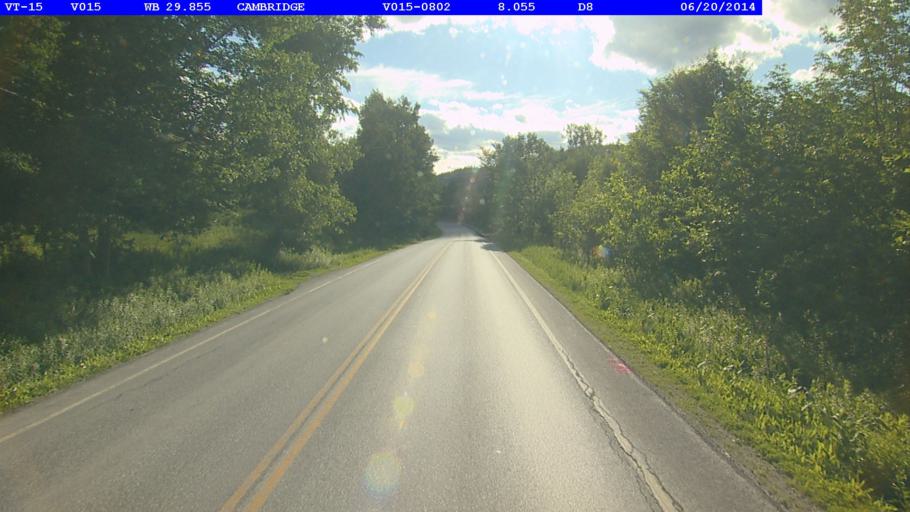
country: US
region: Vermont
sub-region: Lamoille County
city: Johnson
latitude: 44.6666
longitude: -72.7800
